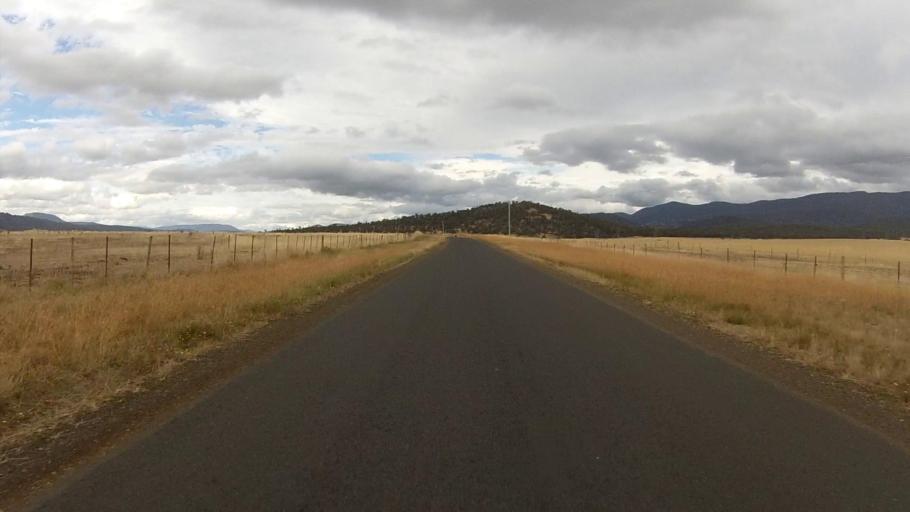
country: AU
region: Tasmania
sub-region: Northern Midlands
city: Evandale
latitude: -41.8269
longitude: 147.7802
